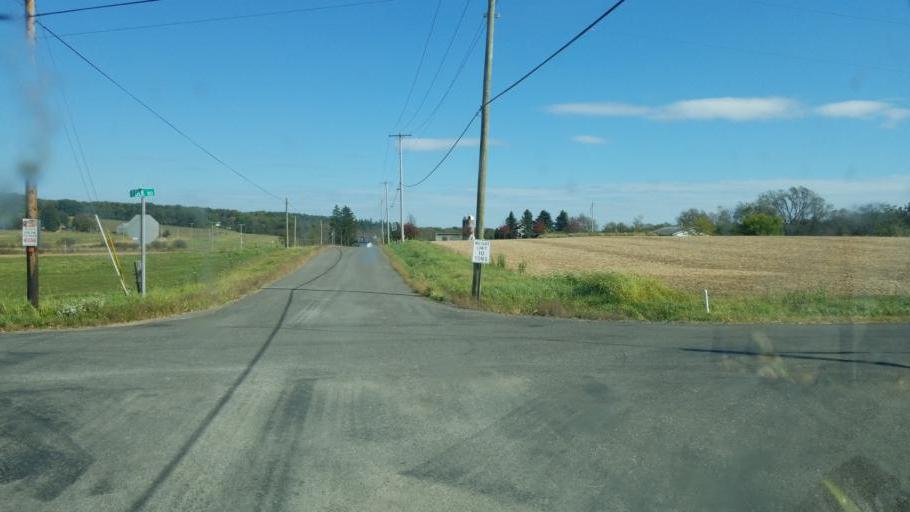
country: US
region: Pennsylvania
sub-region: Mercer County
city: Reynolds Heights
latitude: 41.3280
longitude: -80.2861
